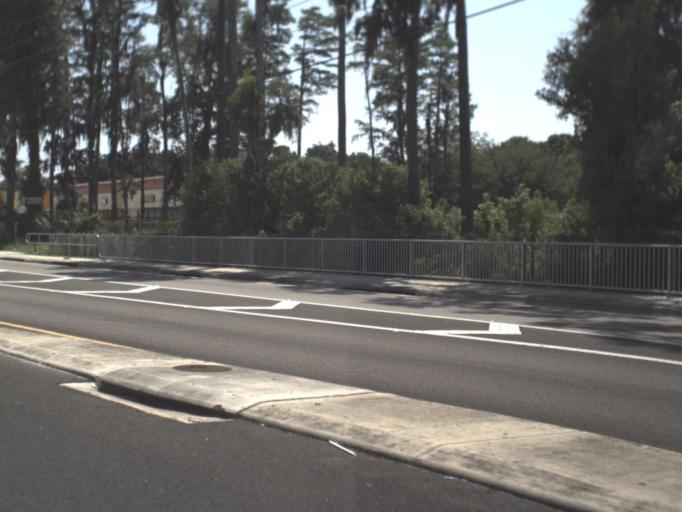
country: US
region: Florida
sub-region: Pinellas County
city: Safety Harbor
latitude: 27.9868
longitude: -82.7298
